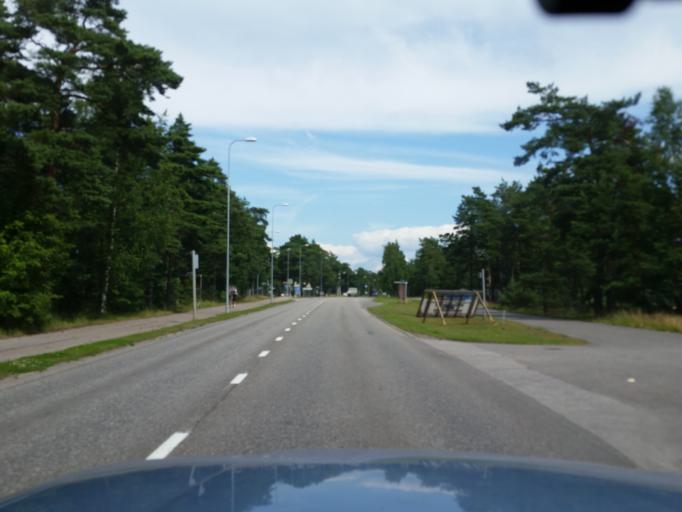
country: FI
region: Uusimaa
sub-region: Raaseporin
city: Hanko
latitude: 59.8367
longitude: 22.9929
